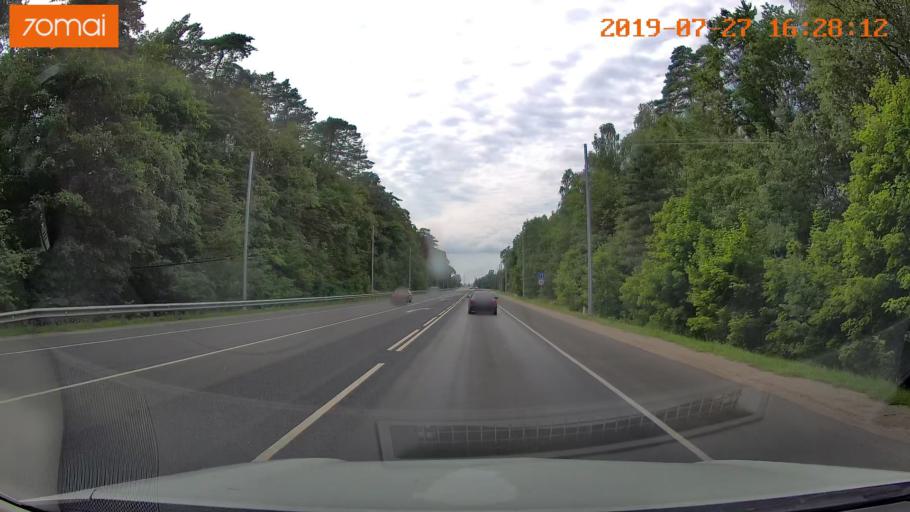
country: RU
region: Kaliningrad
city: Zheleznodorozhnyy
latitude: 54.6471
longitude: 21.3654
